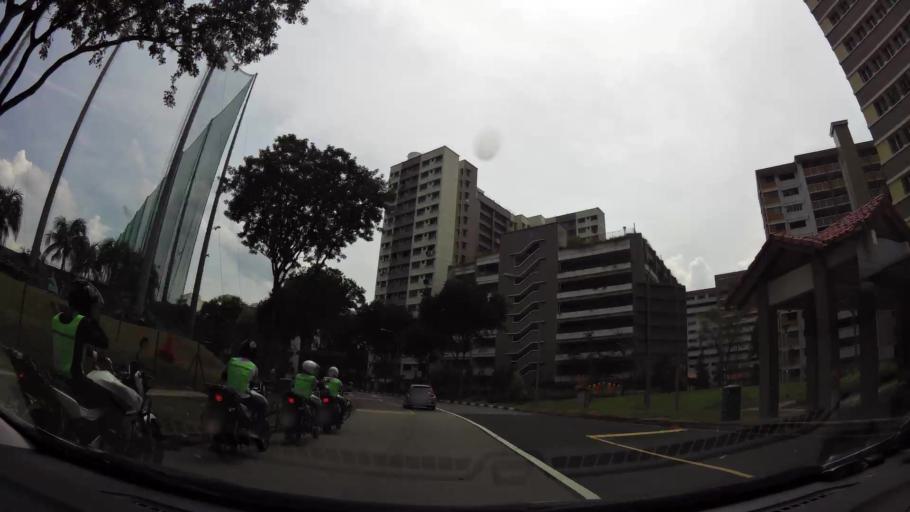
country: MY
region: Johor
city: Johor Bahru
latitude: 1.3655
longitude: 103.7463
